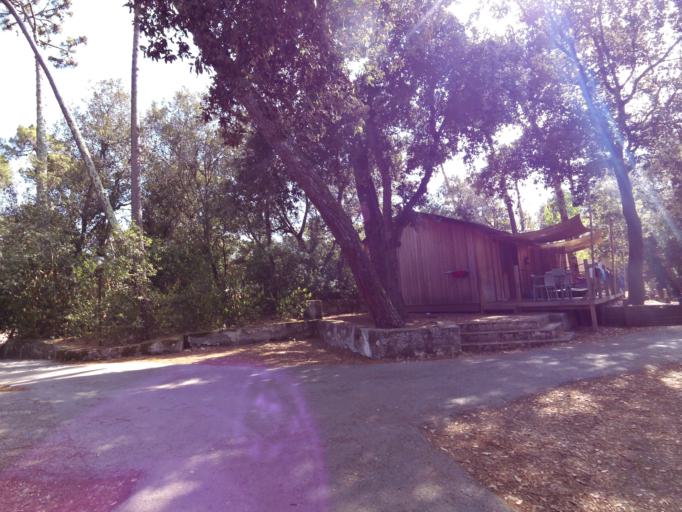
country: IT
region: Tuscany
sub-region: Provincia di Livorno
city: Donoratico
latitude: 43.1529
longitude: 10.5427
